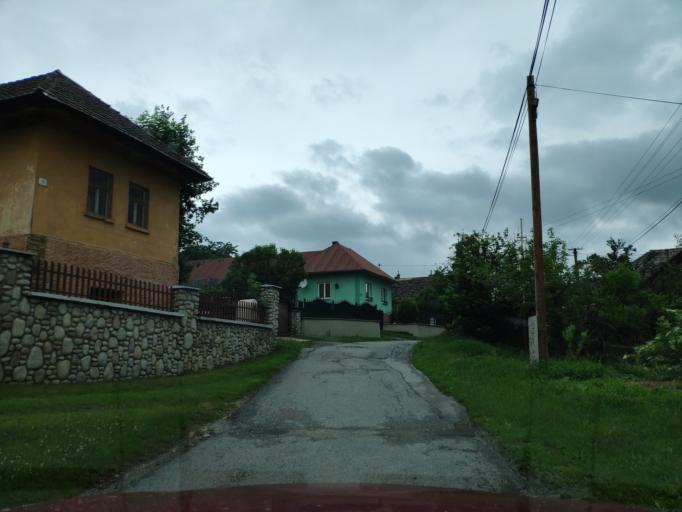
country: SK
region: Presovsky
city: Sabinov
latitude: 49.0432
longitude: 21.0177
